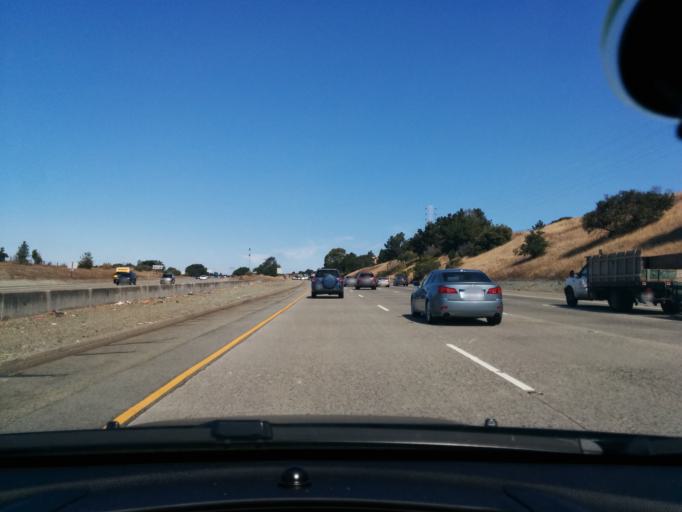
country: US
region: California
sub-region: San Mateo County
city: Highlands-Baywood Park
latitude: 37.5340
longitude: -122.3622
